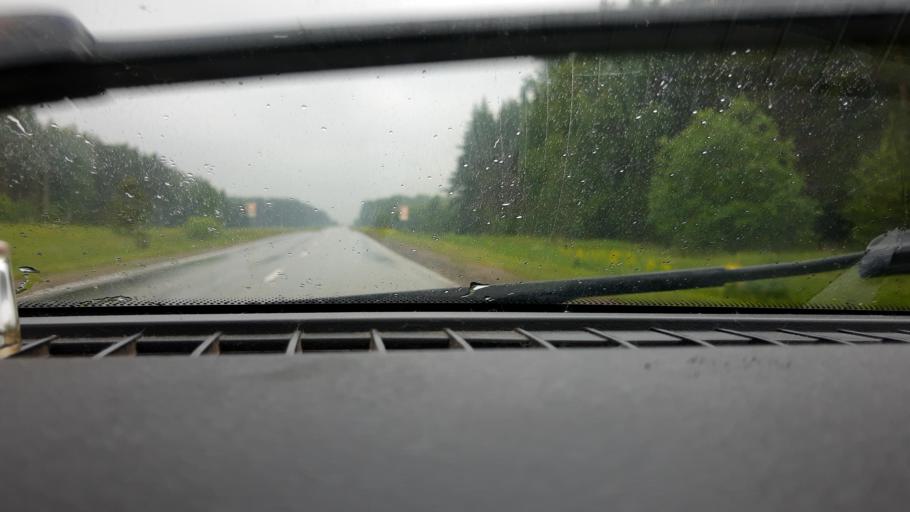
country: RU
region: Bashkortostan
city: Belebey
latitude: 54.2078
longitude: 54.0776
